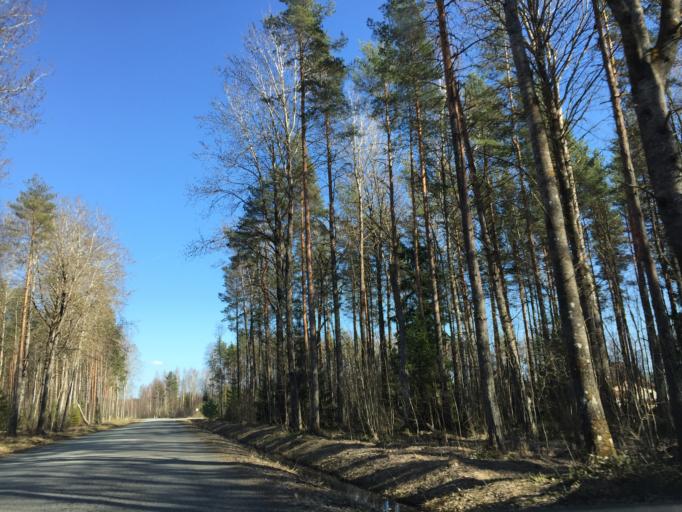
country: EE
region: Ida-Virumaa
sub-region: Johvi vald
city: Johvi
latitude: 59.0133
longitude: 27.5314
